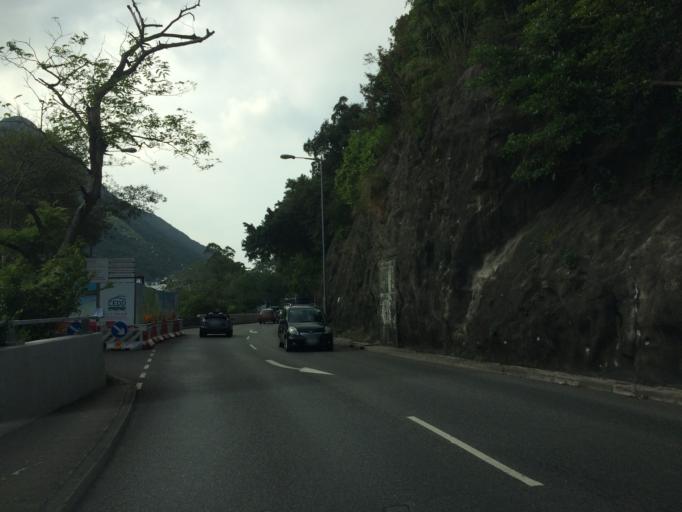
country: HK
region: Wanchai
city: Wan Chai
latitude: 22.2453
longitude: 114.1810
